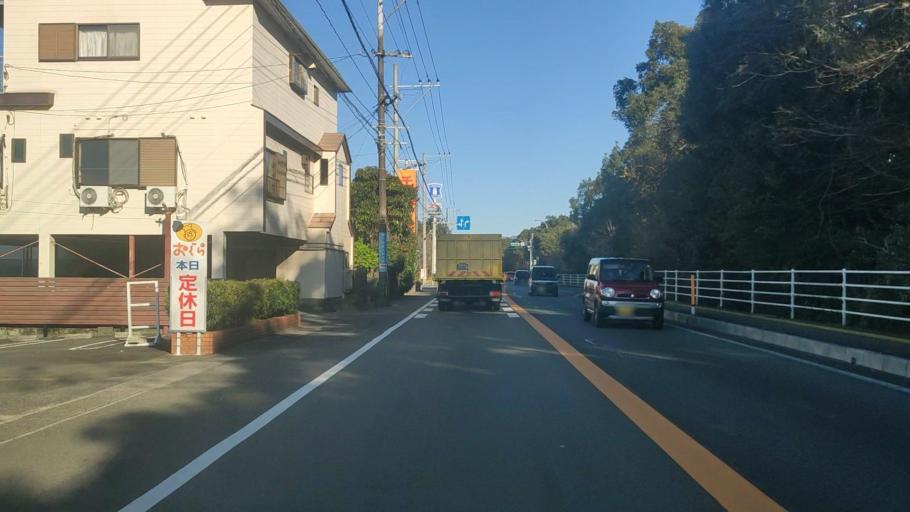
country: JP
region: Miyazaki
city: Nobeoka
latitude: 32.5277
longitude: 131.6821
